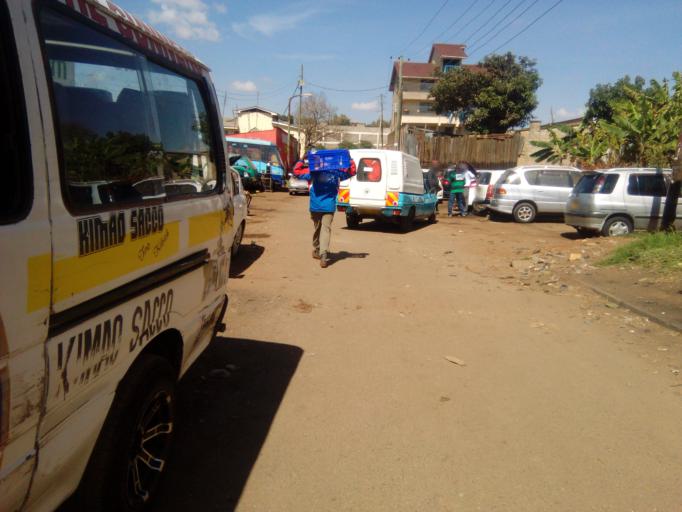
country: KE
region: Nairobi Area
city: Nairobi
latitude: -1.3090
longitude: 36.7790
